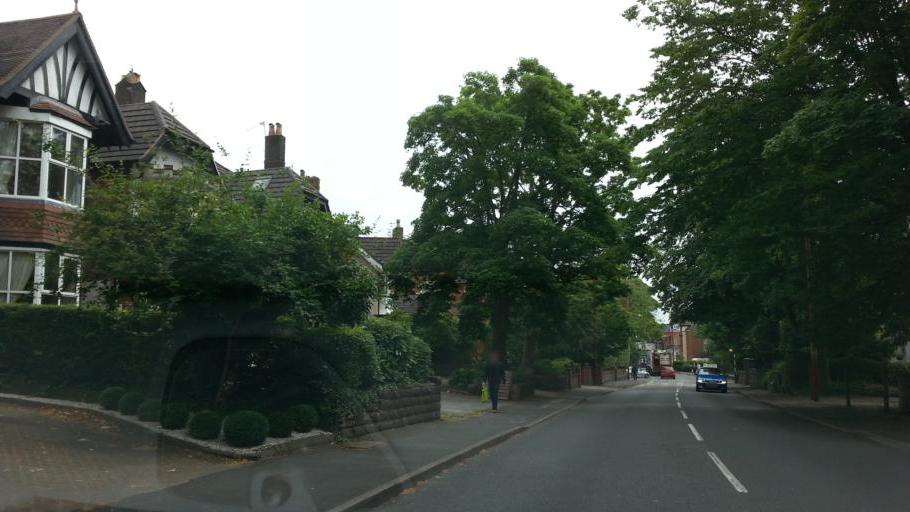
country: GB
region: England
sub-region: City and Borough of Birmingham
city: Bartley Green
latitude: 52.4152
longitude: -1.9368
